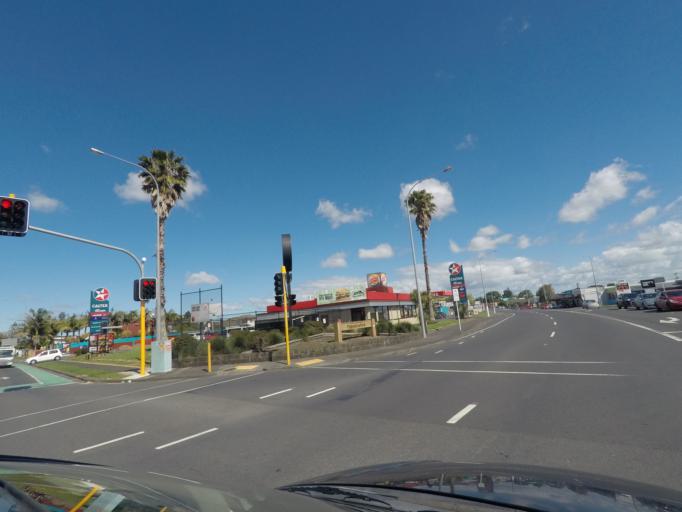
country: NZ
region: Auckland
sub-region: Auckland
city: Manukau City
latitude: -36.9815
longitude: 174.8775
